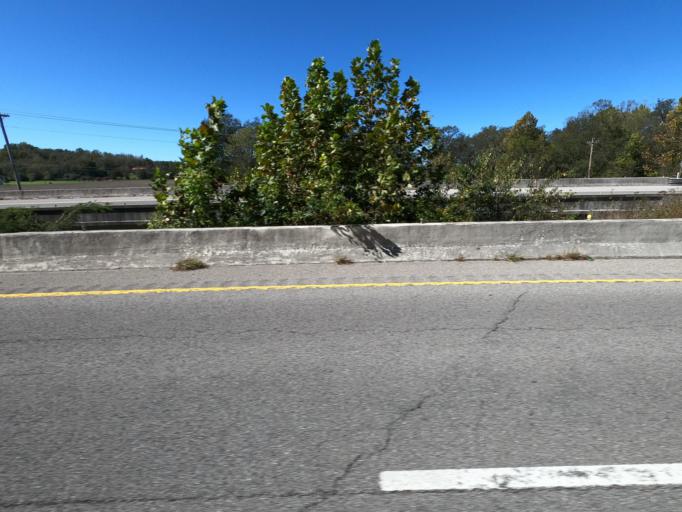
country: US
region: Tennessee
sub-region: Maury County
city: Mount Pleasant
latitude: 35.5035
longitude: -87.2312
